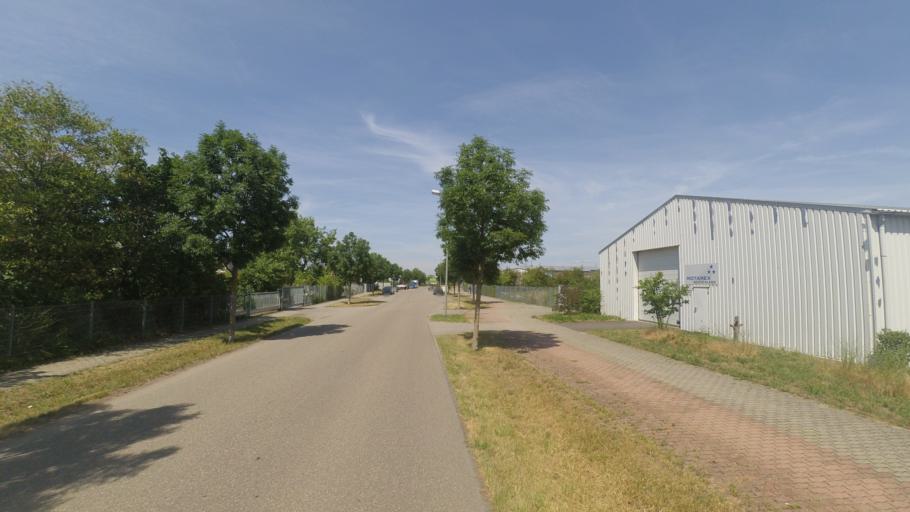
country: DE
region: Rheinland-Pfalz
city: Limburgerhof
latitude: 49.4272
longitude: 8.3918
